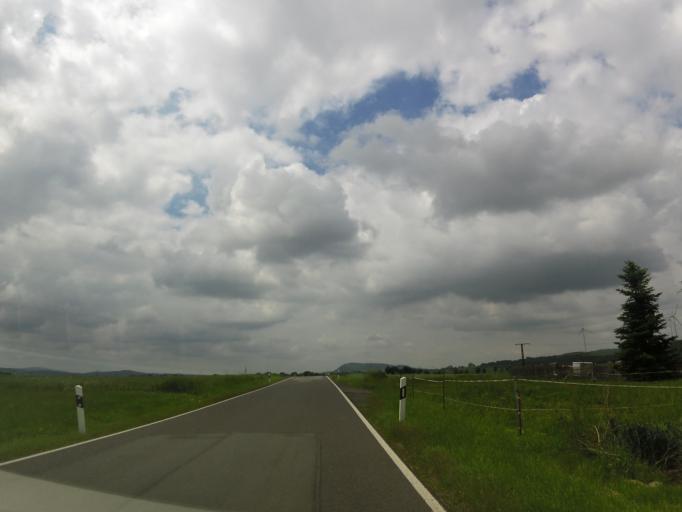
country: DE
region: Thuringia
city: Horselgau
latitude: 50.9353
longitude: 10.5689
